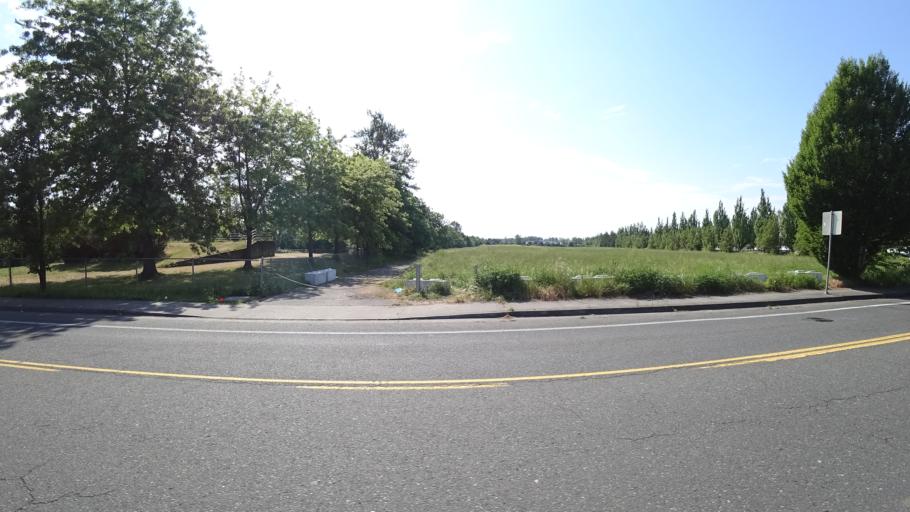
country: US
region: Oregon
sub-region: Multnomah County
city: Fairview
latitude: 45.5569
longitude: -122.5002
